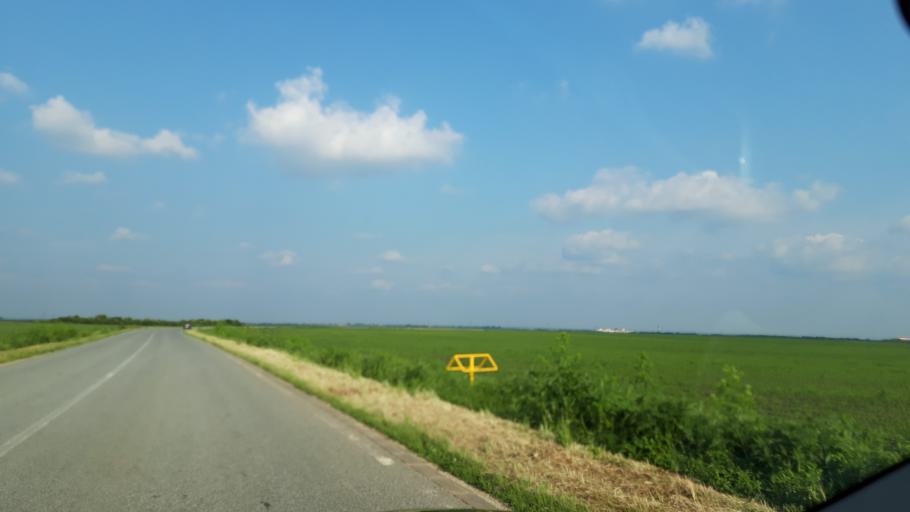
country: RS
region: Autonomna Pokrajina Vojvodina
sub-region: Sremski Okrug
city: Ingija
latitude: 45.0882
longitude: 20.1035
